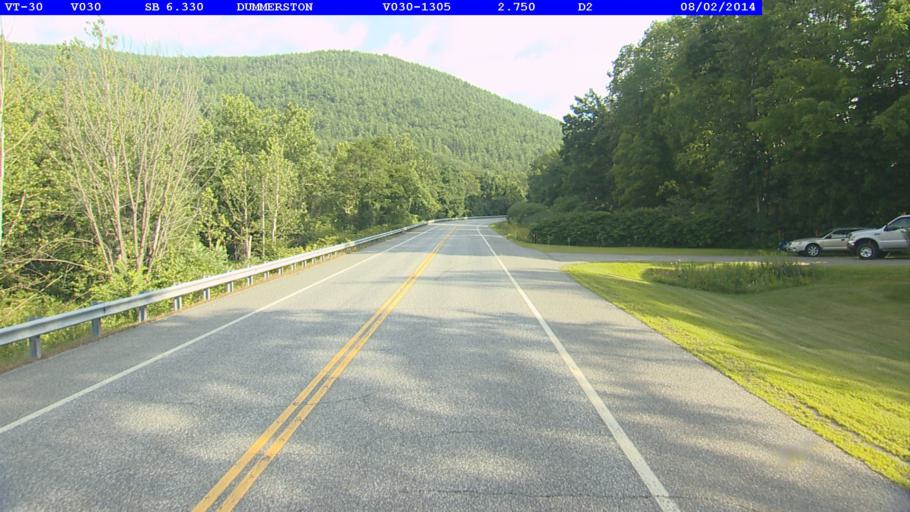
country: US
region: Vermont
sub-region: Windham County
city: Newfane
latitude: 42.9320
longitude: -72.6118
